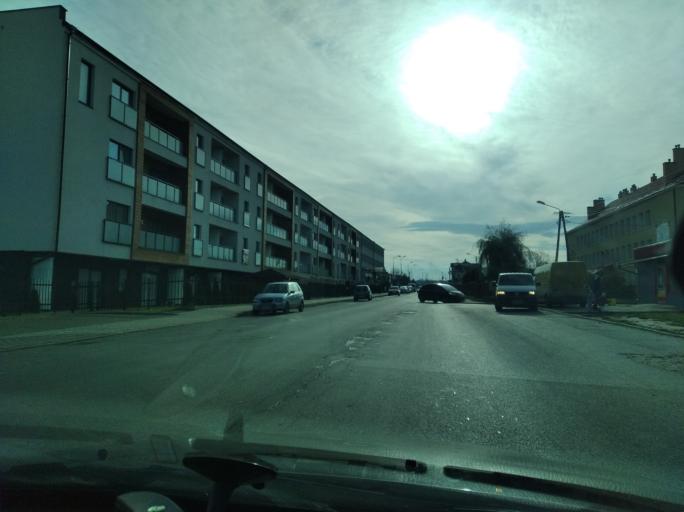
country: PL
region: Subcarpathian Voivodeship
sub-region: Powiat ropczycko-sedziszowski
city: Sedziszow Malopolski
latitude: 50.0715
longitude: 21.6898
